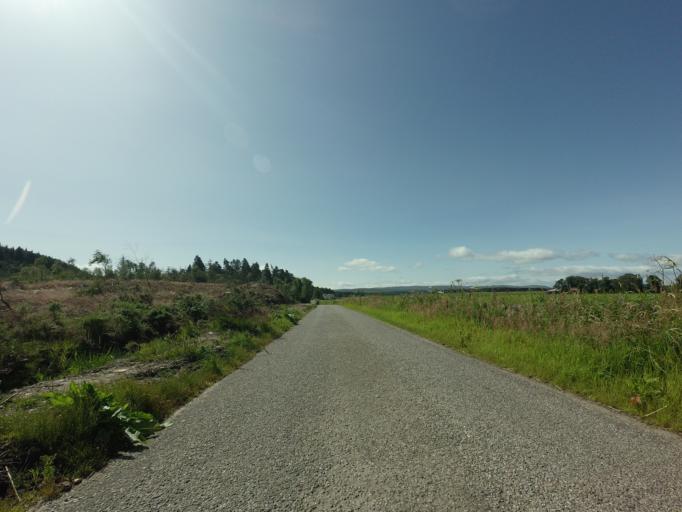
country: GB
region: Scotland
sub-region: Highland
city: Nairn
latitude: 57.5293
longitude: -3.8621
